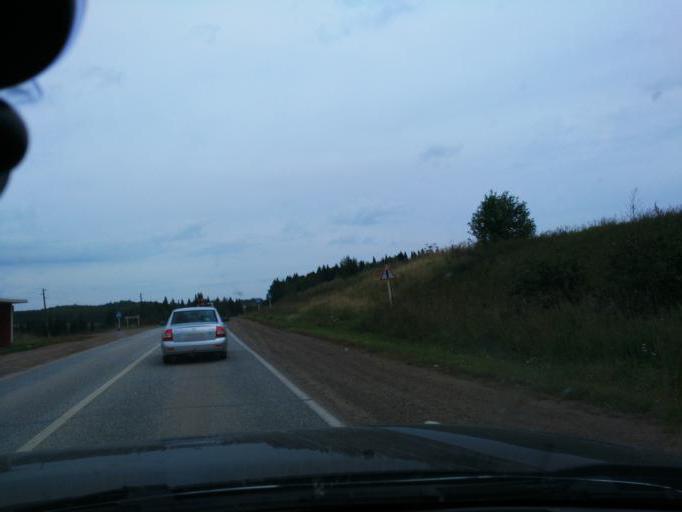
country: RU
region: Perm
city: Chernushka
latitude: 56.5658
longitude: 56.1190
